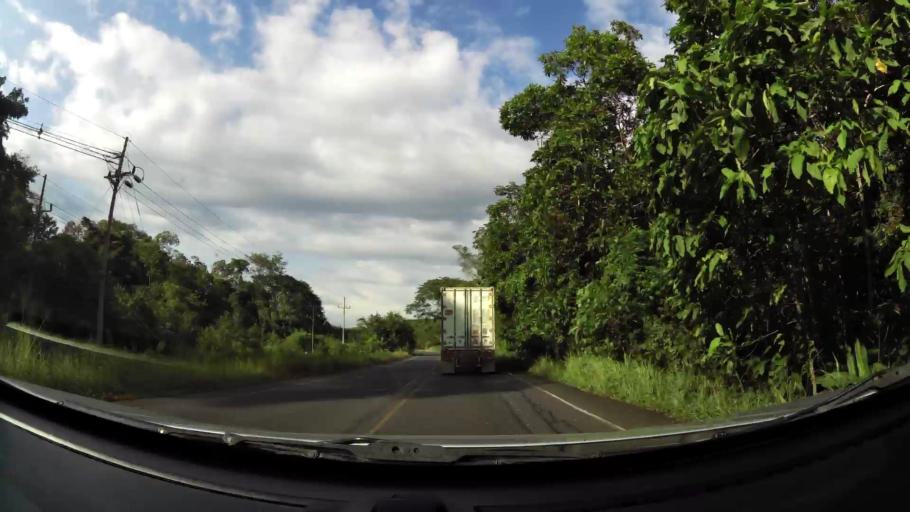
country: CR
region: Alajuela
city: Orotina
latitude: 9.7781
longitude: -84.6069
